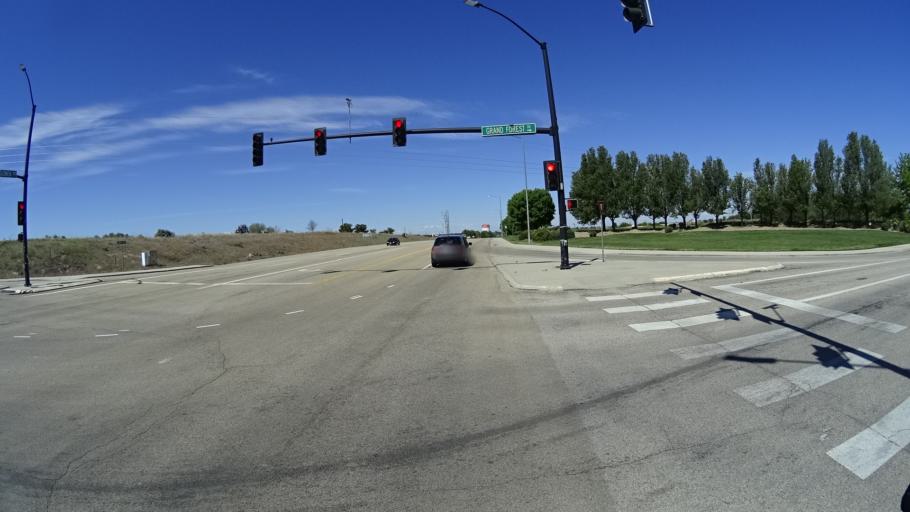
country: US
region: Idaho
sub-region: Ada County
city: Boise
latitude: 43.5406
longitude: -116.1479
